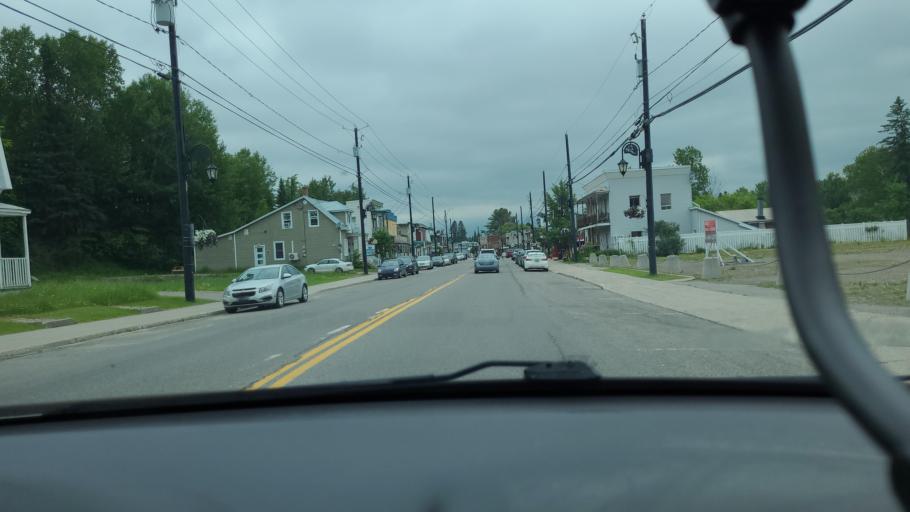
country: CA
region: Quebec
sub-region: Laurentides
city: Riviere-Rouge
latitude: 46.4102
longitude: -74.8705
